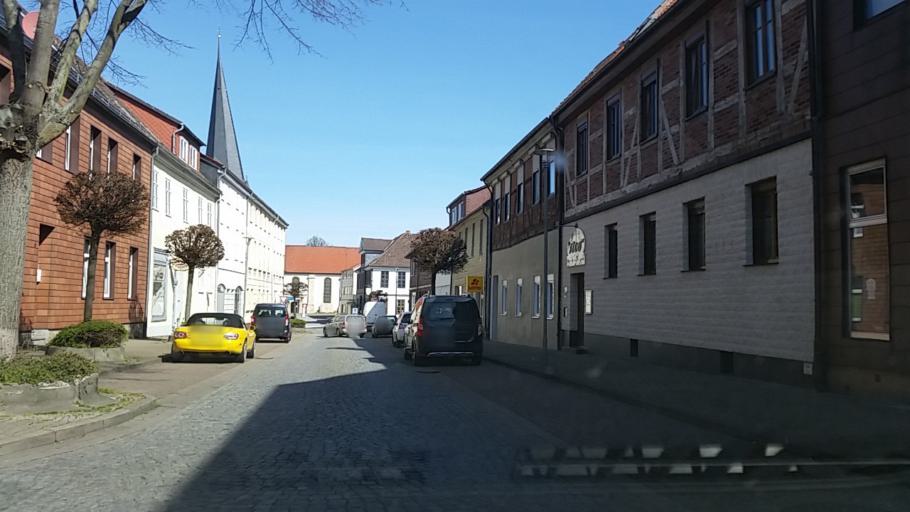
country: DE
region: Lower Saxony
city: Schoppenstedt
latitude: 52.1435
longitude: 10.7759
